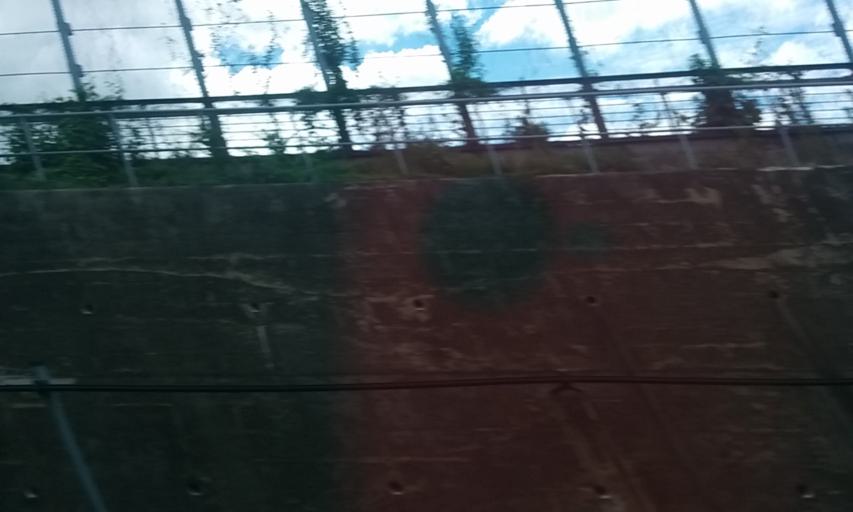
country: JP
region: Fukushima
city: Motomiya
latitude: 37.4547
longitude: 140.4078
